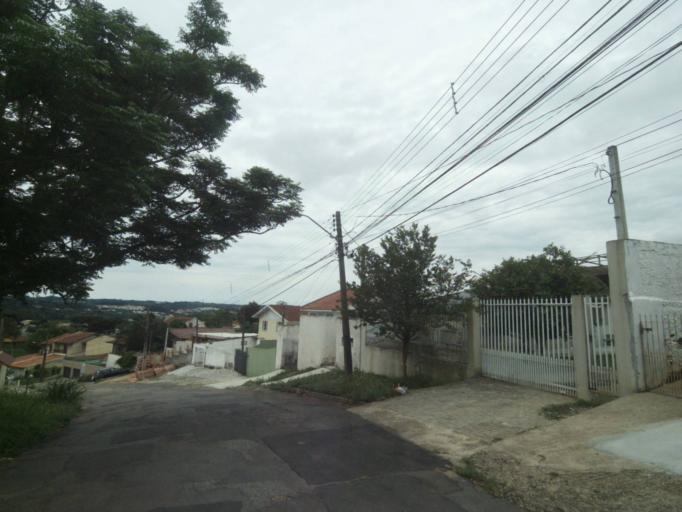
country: BR
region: Parana
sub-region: Curitiba
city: Curitiba
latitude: -25.3921
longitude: -49.2919
